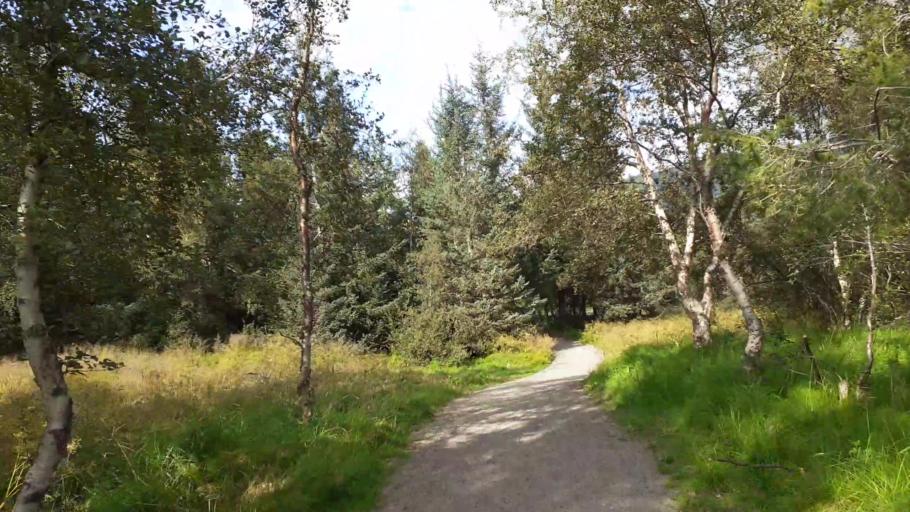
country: IS
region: Northeast
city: Akureyri
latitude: 65.6459
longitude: -18.0862
